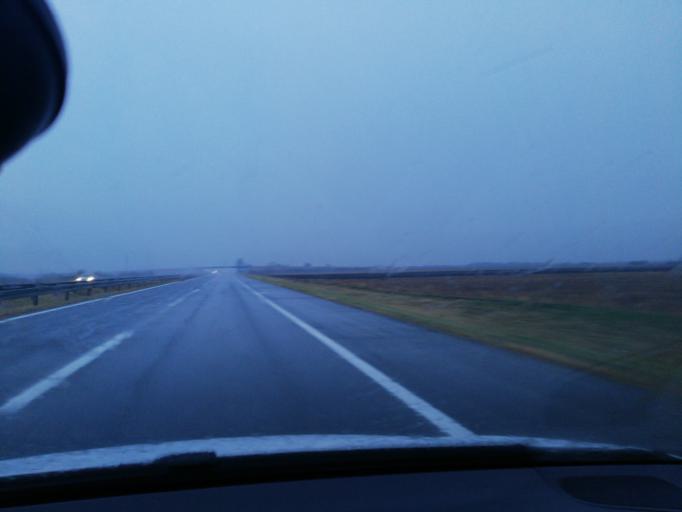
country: RS
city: Sasinci
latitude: 44.9731
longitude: 19.7575
